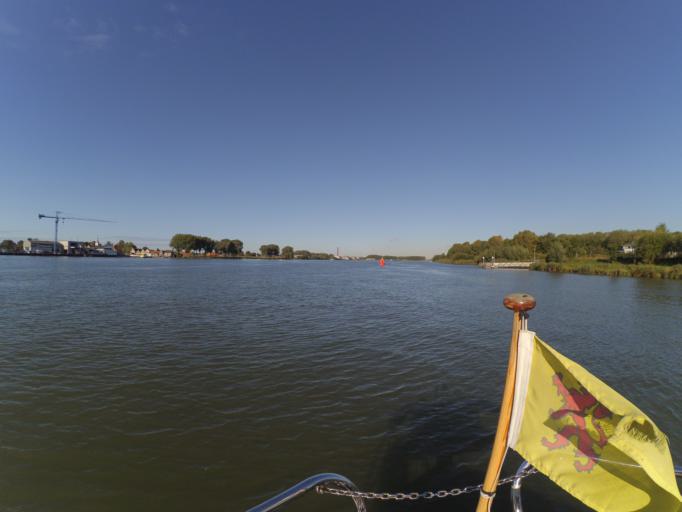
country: NL
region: South Holland
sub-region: Gemeente Zwijndrecht
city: Heerjansdam
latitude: 51.8084
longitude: 4.5815
